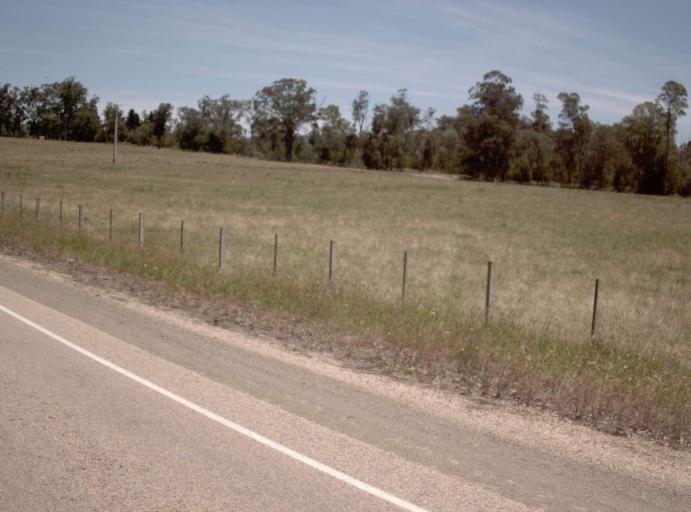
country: AU
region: Victoria
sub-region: East Gippsland
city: Lakes Entrance
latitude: -37.6804
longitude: 147.8476
